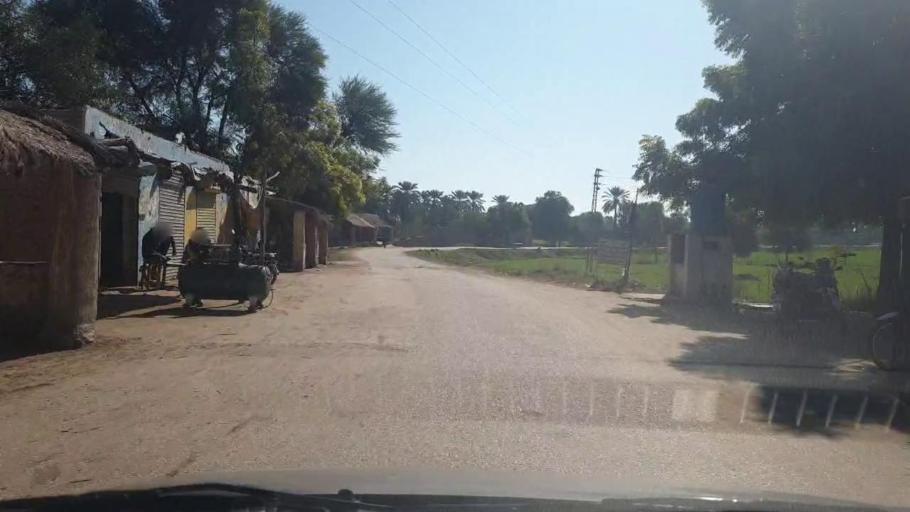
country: PK
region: Sindh
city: Bozdar
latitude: 27.1178
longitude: 68.6345
